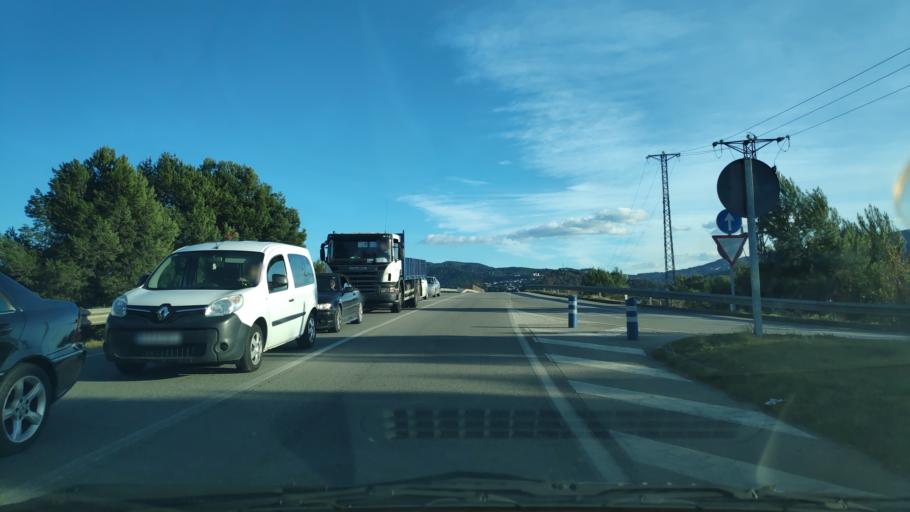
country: ES
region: Catalonia
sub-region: Provincia de Barcelona
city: Mollet del Valles
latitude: 41.5326
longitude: 2.2152
